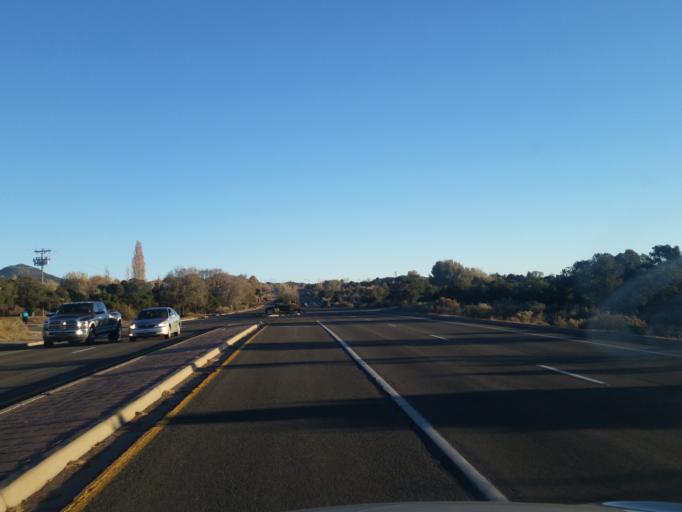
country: US
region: New Mexico
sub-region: Santa Fe County
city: Santa Fe
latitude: 35.6476
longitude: -105.9341
